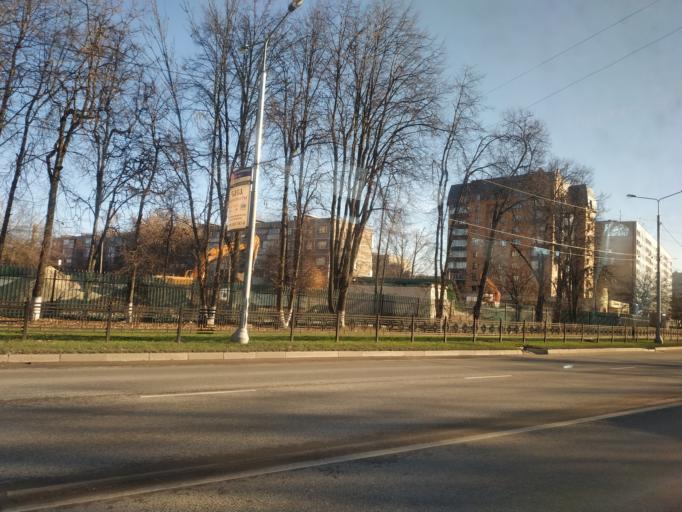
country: RU
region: Moskovskaya
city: Domodedovo
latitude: 55.4336
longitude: 37.7669
